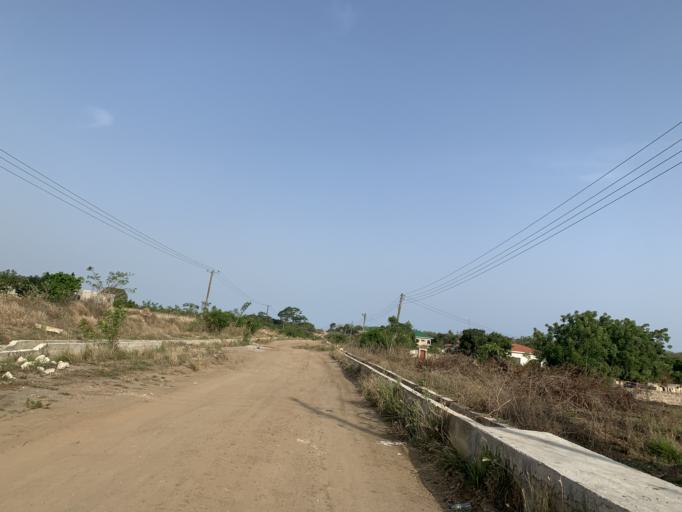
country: GH
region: Central
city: Winneba
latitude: 5.3811
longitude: -0.6215
